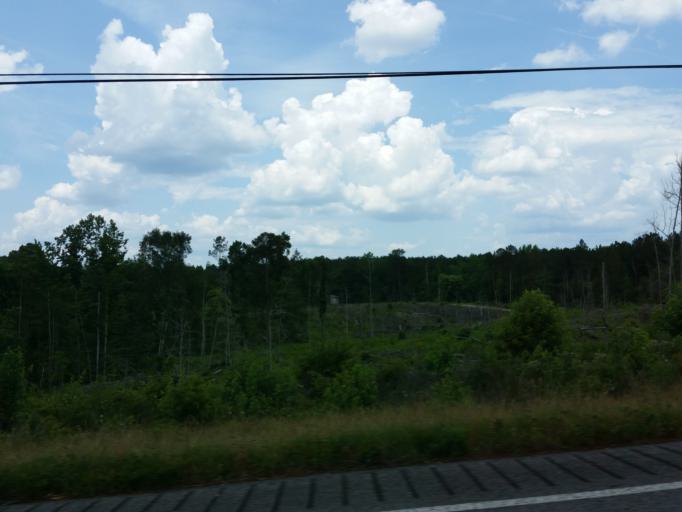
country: US
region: Alabama
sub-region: Sumter County
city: York
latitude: 32.4139
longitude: -88.2340
